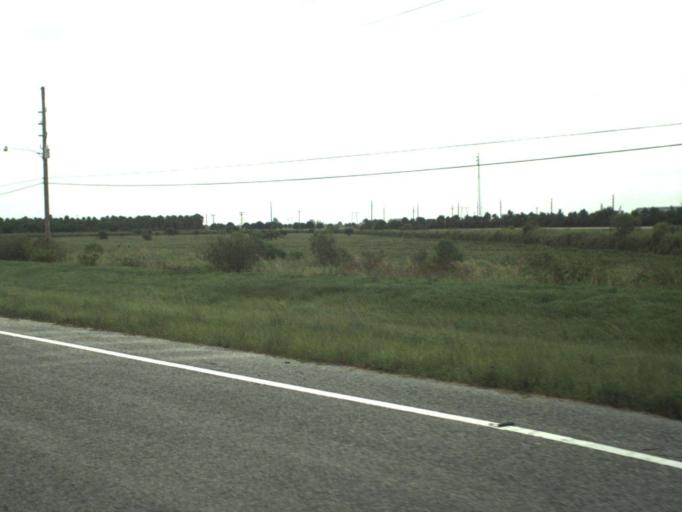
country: US
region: Florida
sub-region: Saint Lucie County
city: Fort Pierce South
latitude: 27.3761
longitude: -80.4855
